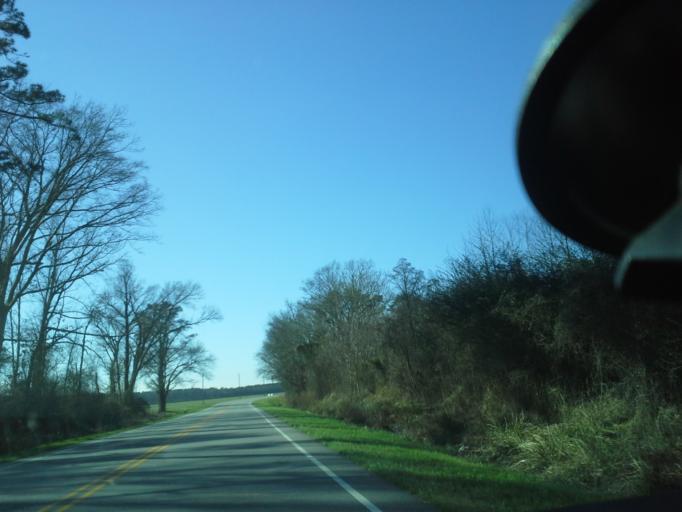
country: US
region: North Carolina
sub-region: Beaufort County
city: Belhaven
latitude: 35.5280
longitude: -76.7561
